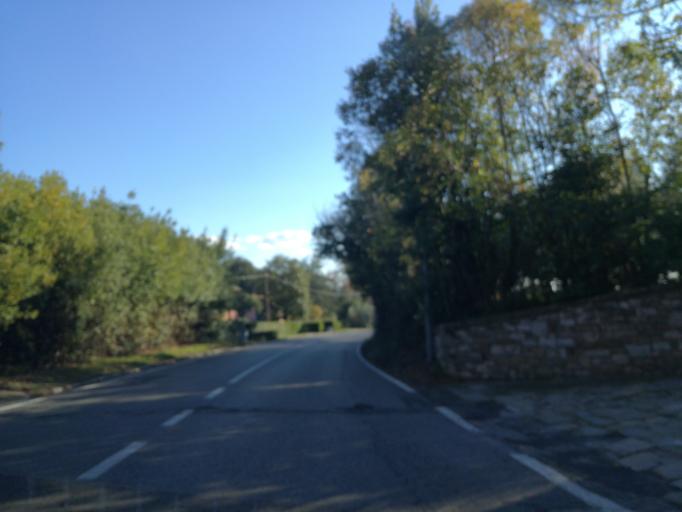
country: IT
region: Umbria
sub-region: Provincia di Perugia
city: Perugia
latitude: 43.0837
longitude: 12.4005
